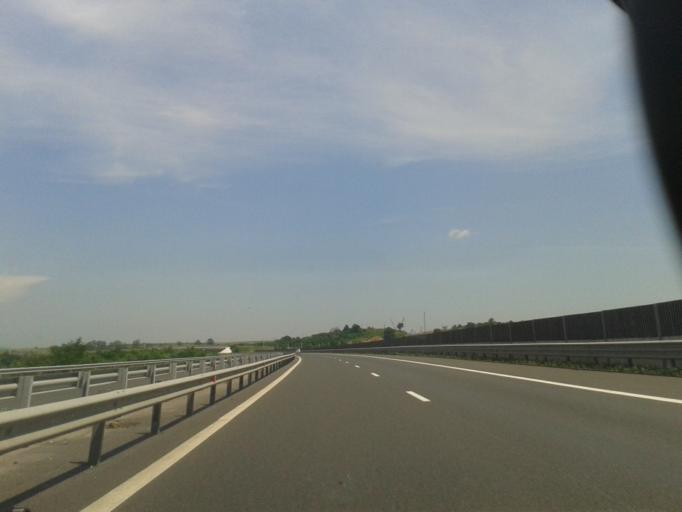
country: RO
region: Hunedoara
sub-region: Comuna Turdas
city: Turdas
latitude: 45.8369
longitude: 23.1100
